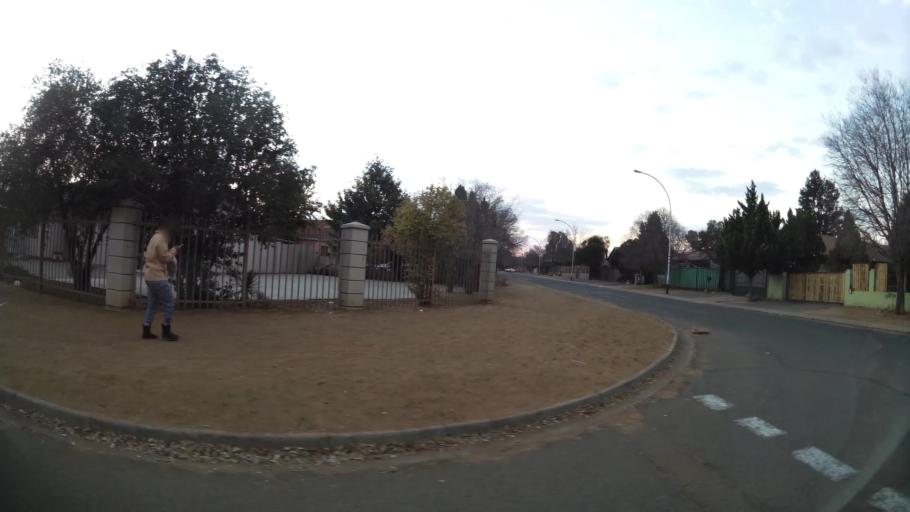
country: ZA
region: Orange Free State
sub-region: Mangaung Metropolitan Municipality
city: Bloemfontein
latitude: -29.1697
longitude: 26.1881
